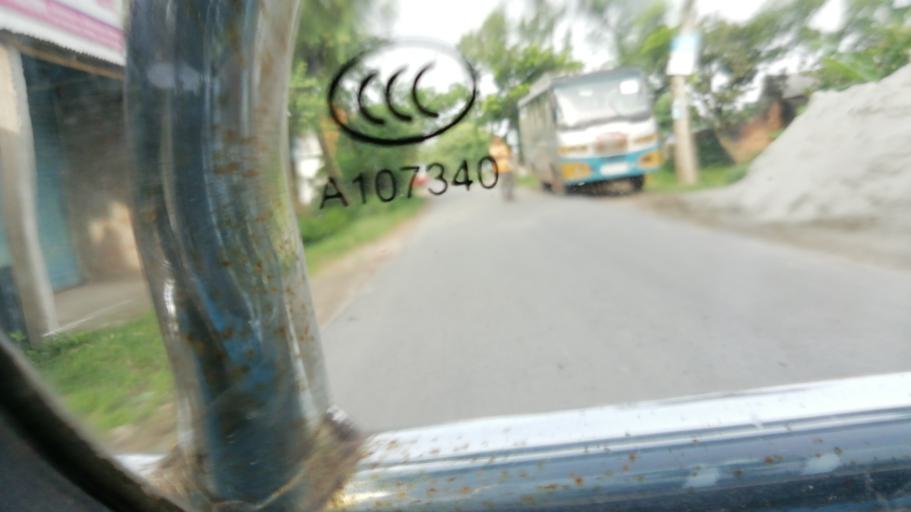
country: BD
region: Khulna
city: Kesabpur
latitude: 23.0310
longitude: 89.2729
